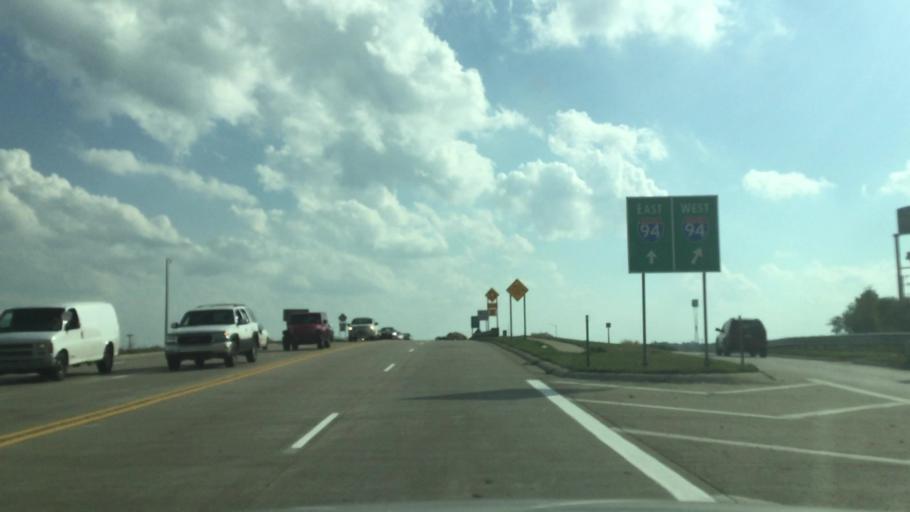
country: US
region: Michigan
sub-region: Kalamazoo County
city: Eastwood
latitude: 42.2609
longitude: -85.5311
